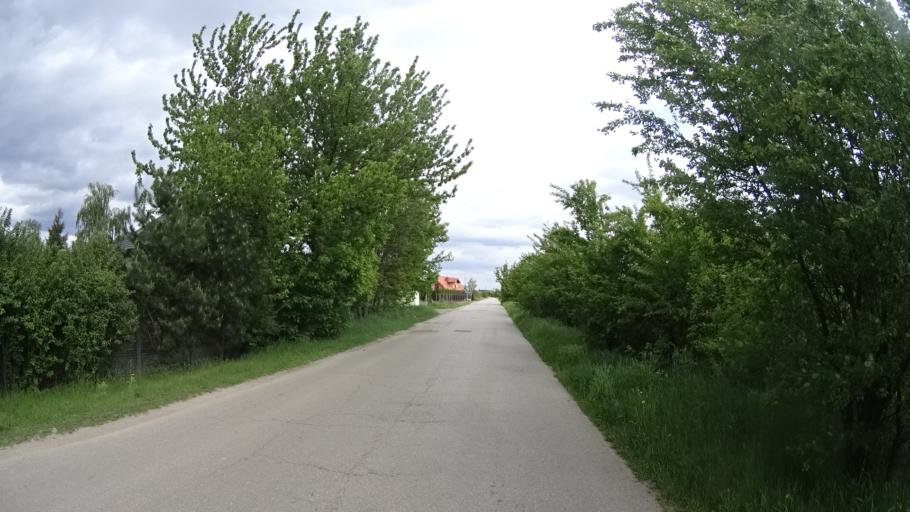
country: PL
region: Masovian Voivodeship
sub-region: Powiat pruszkowski
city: Piastow
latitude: 52.2066
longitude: 20.8376
